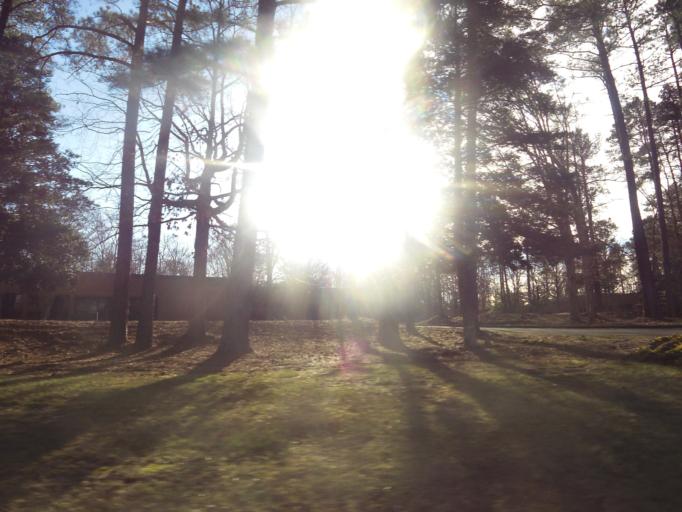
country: US
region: Virginia
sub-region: Henrico County
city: Short Pump
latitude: 37.6531
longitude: -77.5807
